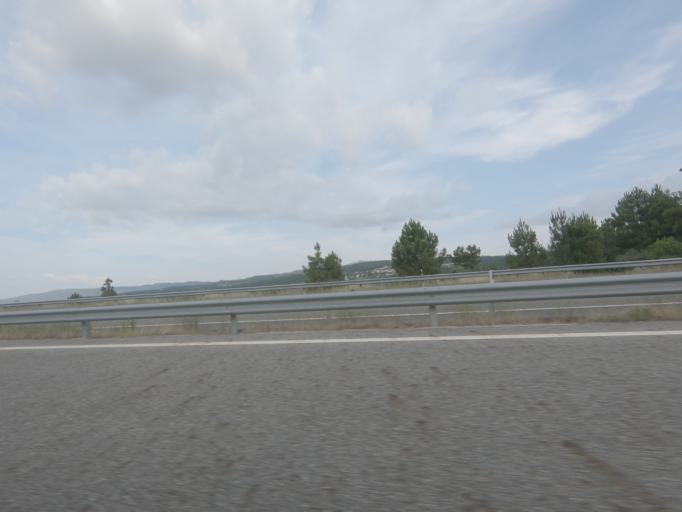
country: PT
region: Vila Real
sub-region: Chaves
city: Chaves
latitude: 41.6926
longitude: -7.5564
